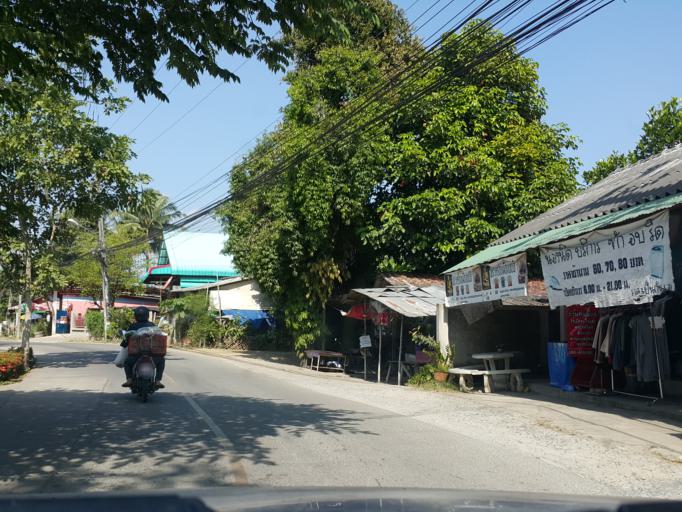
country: TH
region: Chiang Mai
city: San Sai
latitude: 18.8348
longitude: 99.0201
